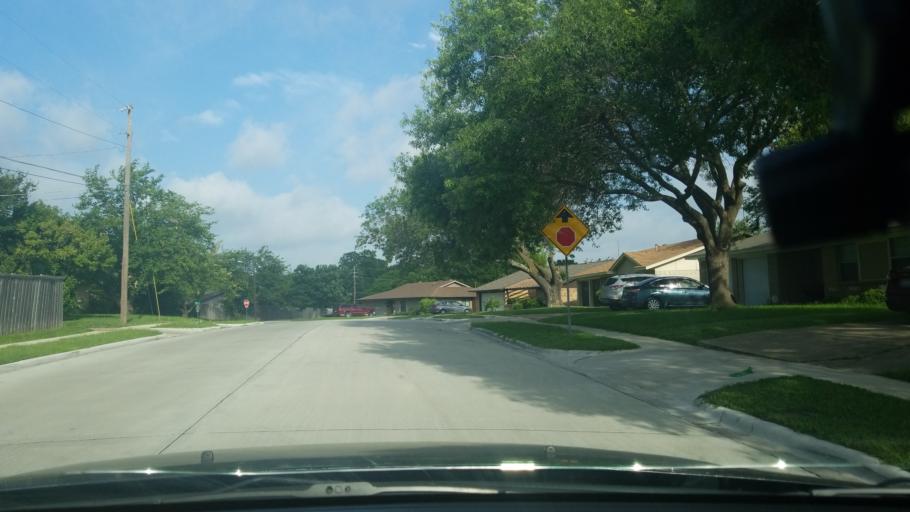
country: US
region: Texas
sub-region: Dallas County
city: Mesquite
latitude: 32.7717
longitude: -96.6387
